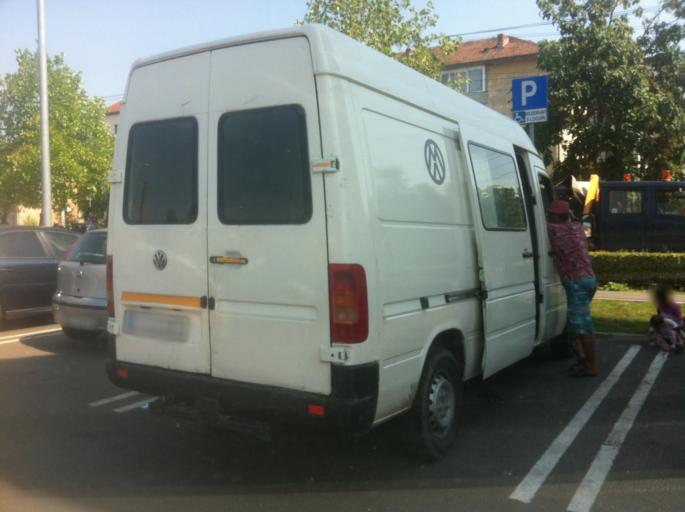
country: RO
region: Timis
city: Timisoara
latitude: 45.7645
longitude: 21.2461
